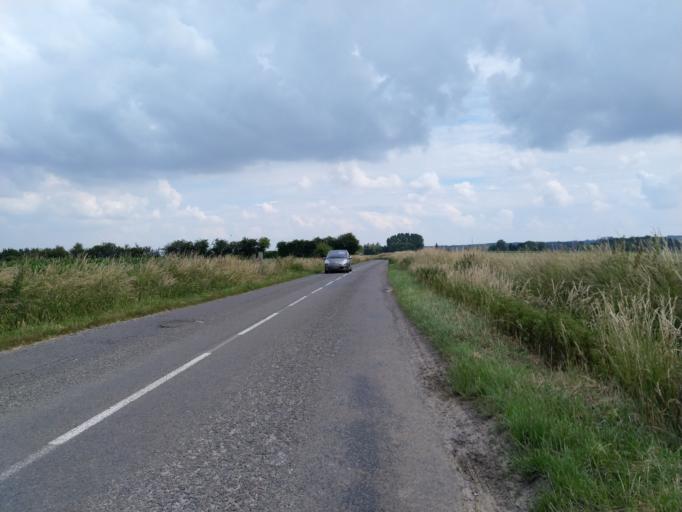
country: FR
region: Nord-Pas-de-Calais
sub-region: Departement du Nord
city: Boussois
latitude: 50.3293
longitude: 4.0085
